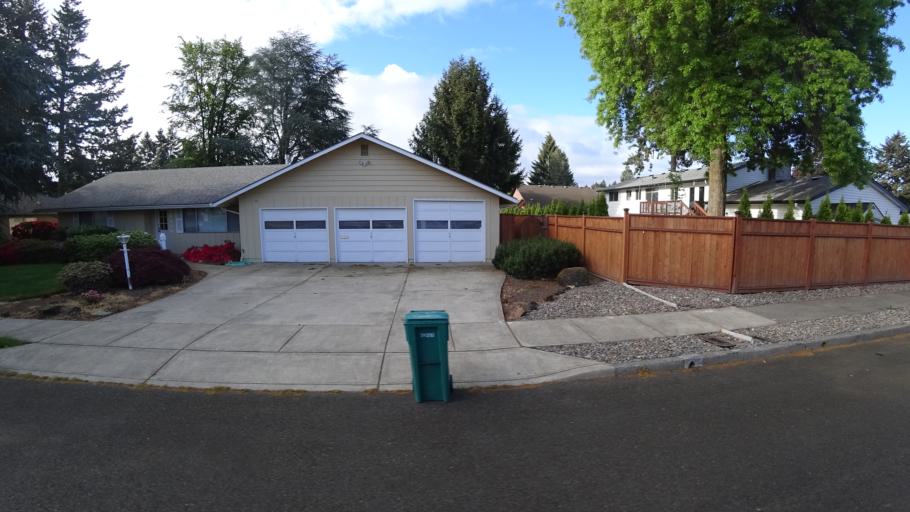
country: US
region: Oregon
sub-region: Washington County
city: Beaverton
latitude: 45.4728
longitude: -122.8246
